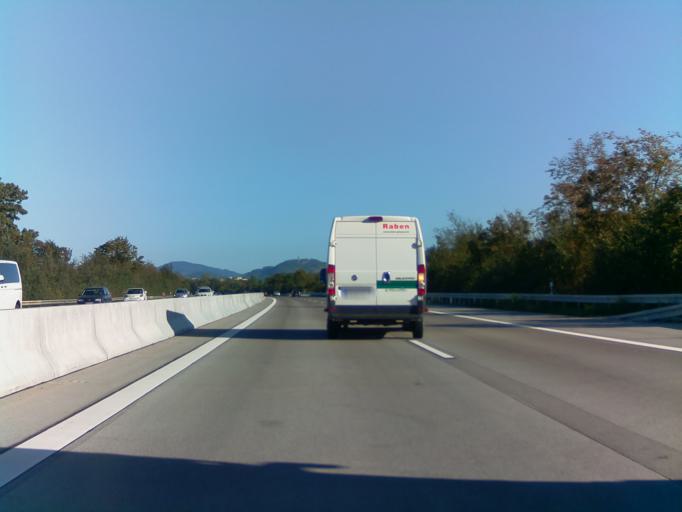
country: DE
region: Baden-Wuerttemberg
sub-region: Karlsruhe Region
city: Hemsbach
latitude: 49.5735
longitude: 8.6349
